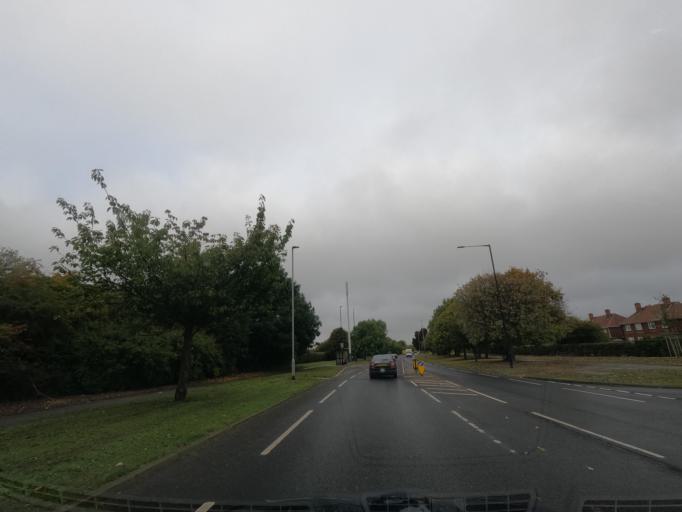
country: GB
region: England
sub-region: Middlesbrough
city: Nunthorpe
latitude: 54.5564
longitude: -1.1872
